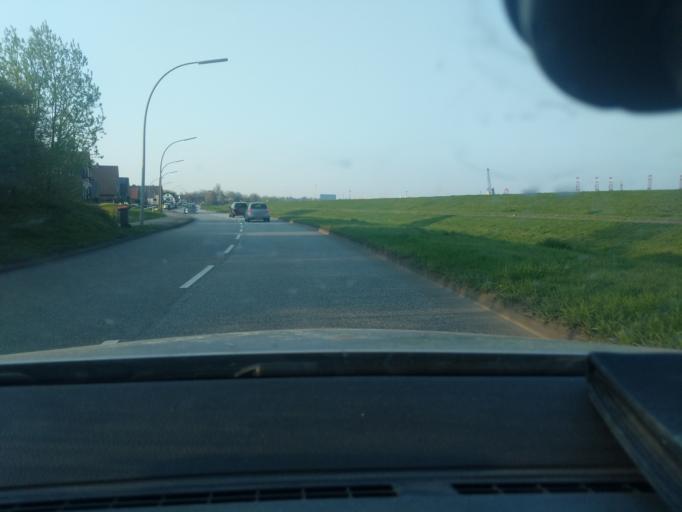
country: DE
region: Hamburg
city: Altona
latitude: 53.5211
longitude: 9.8867
